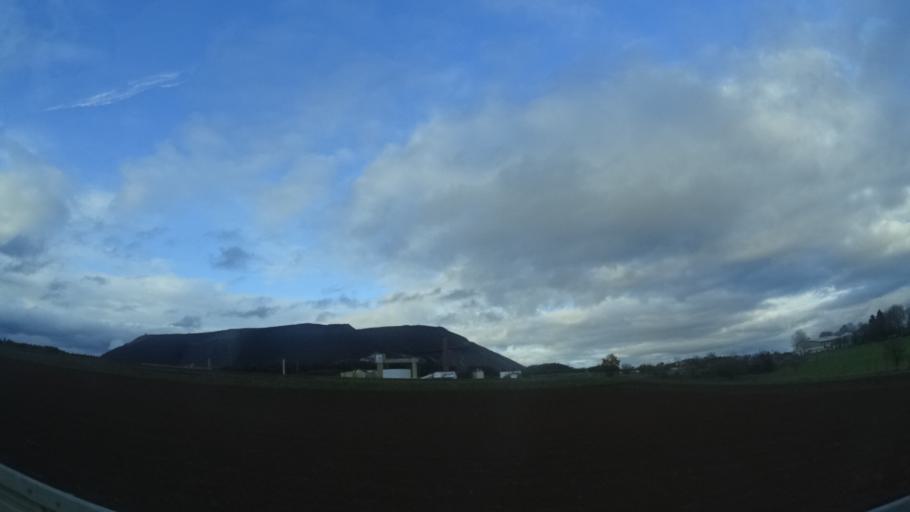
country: DE
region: Hesse
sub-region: Regierungsbezirk Kassel
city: Neuhof
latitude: 50.4532
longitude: 9.5960
